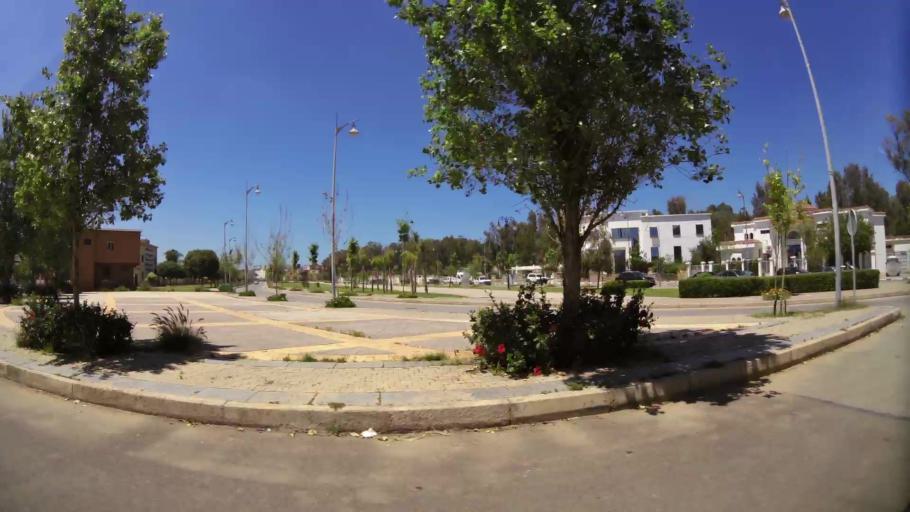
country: MA
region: Oriental
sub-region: Berkane-Taourirt
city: Madagh
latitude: 35.0811
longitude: -2.2175
